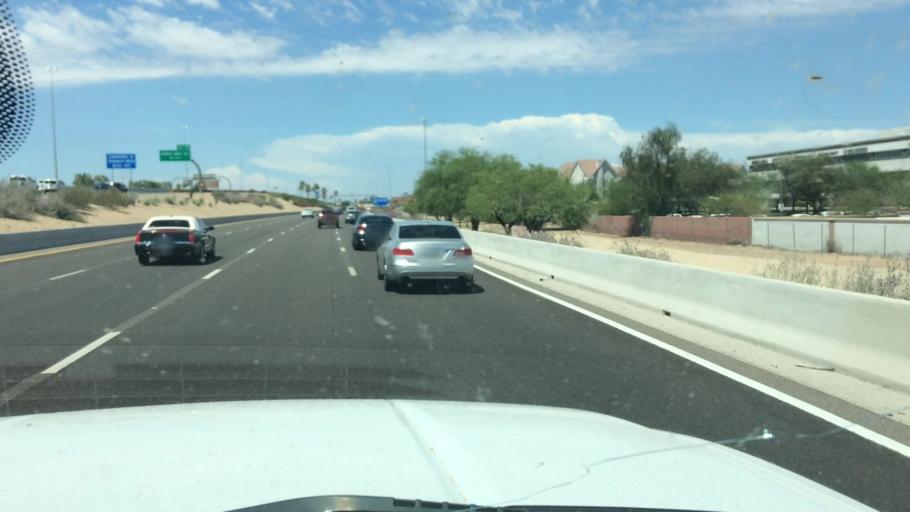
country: US
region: Arizona
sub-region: Maricopa County
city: Sun City
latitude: 33.6342
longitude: -112.2385
